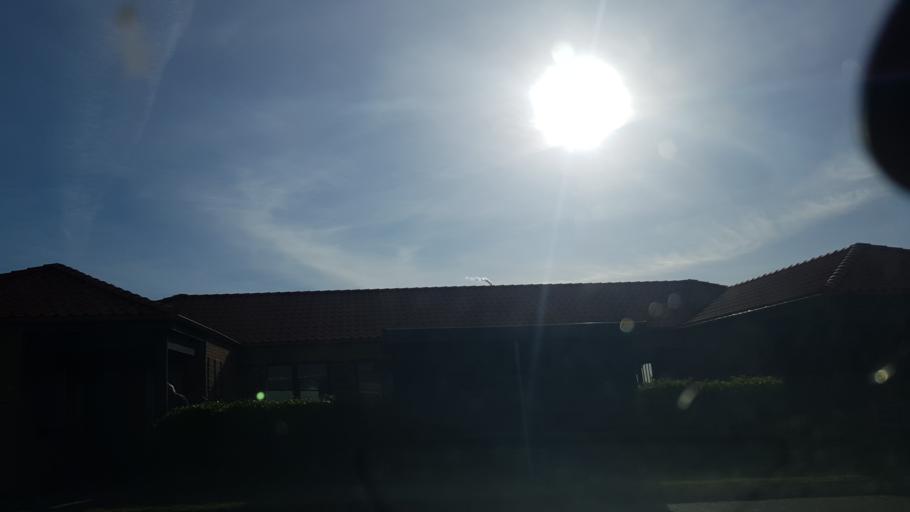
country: DK
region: Zealand
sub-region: Slagelse Kommune
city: Korsor
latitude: 55.3273
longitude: 11.1694
